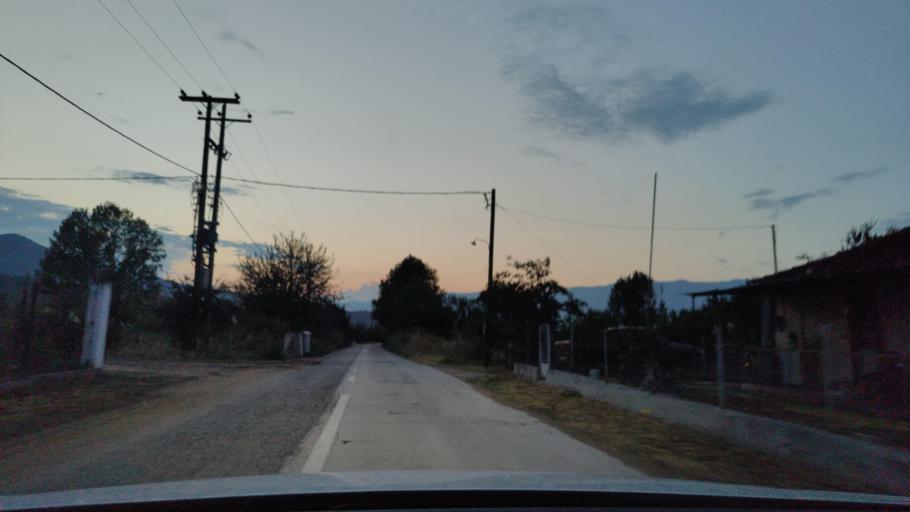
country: GR
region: Central Macedonia
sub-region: Nomos Serron
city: Chrysochorafa
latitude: 41.1813
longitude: 23.1074
